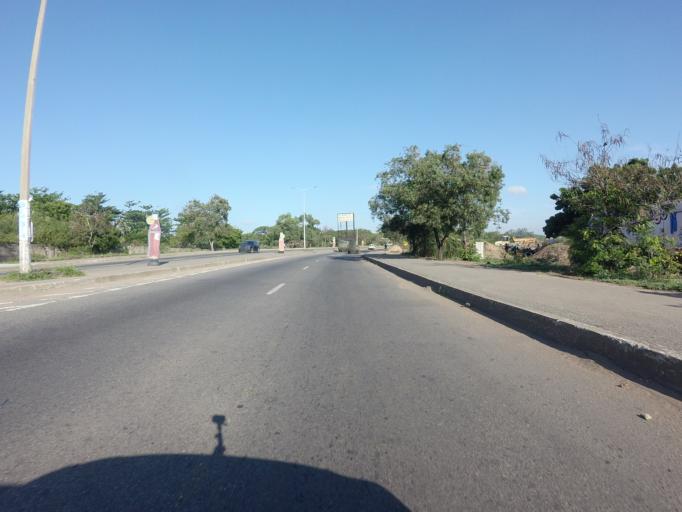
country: GH
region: Greater Accra
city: Accra
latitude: 5.5411
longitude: -0.2247
